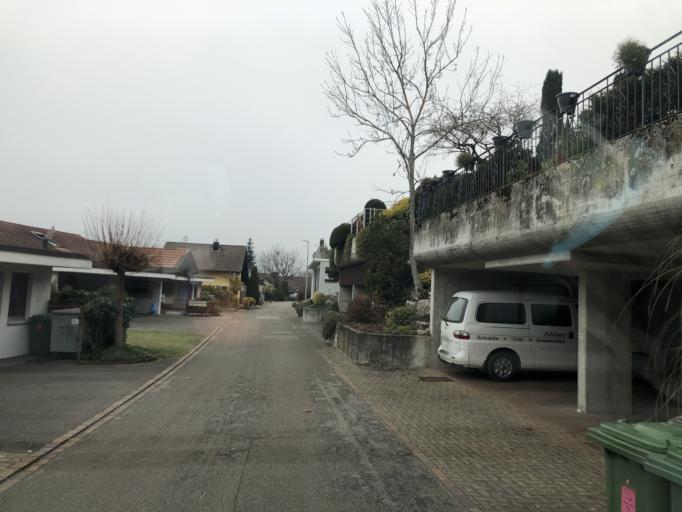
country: CH
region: Aargau
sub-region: Bezirk Baden
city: Gebenstorf
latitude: 47.4820
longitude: 8.2440
